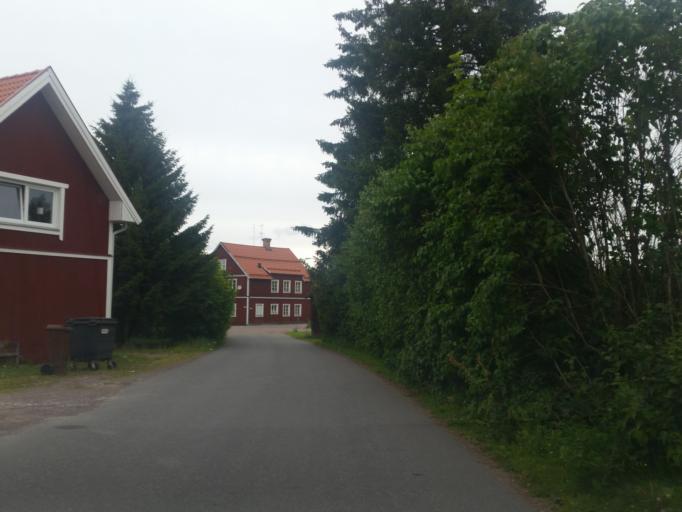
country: SE
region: Dalarna
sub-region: Leksand Municipality
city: Smedby
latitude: 60.6763
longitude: 15.0952
